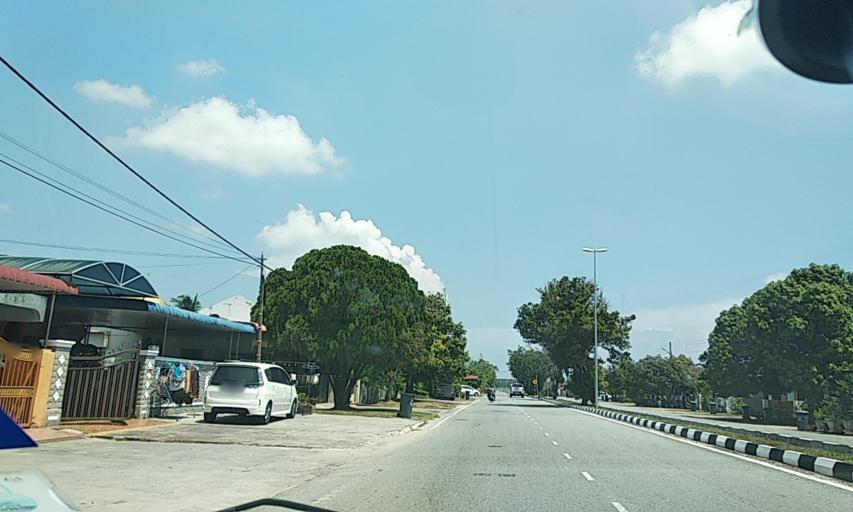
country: MY
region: Kedah
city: Sungai Petani
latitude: 5.6363
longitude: 100.4720
